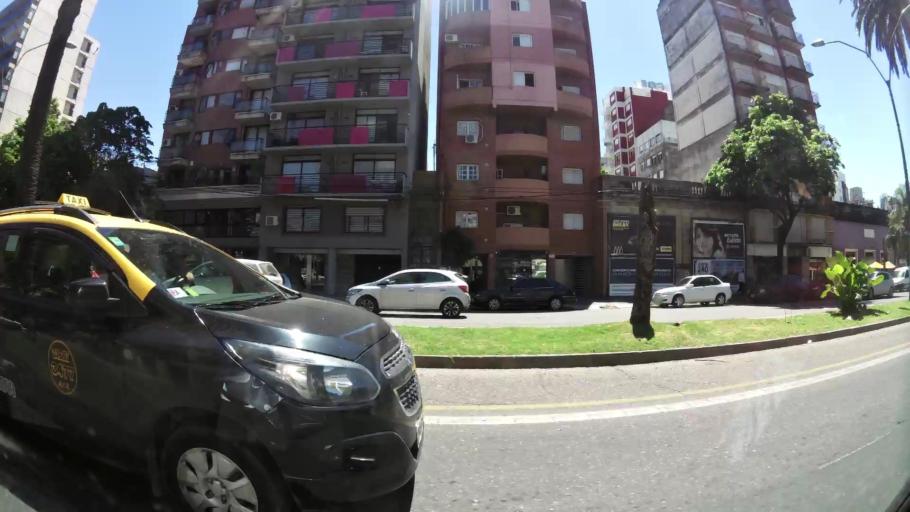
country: AR
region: Santa Fe
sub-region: Departamento de Rosario
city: Rosario
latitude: -32.9419
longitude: -60.6657
